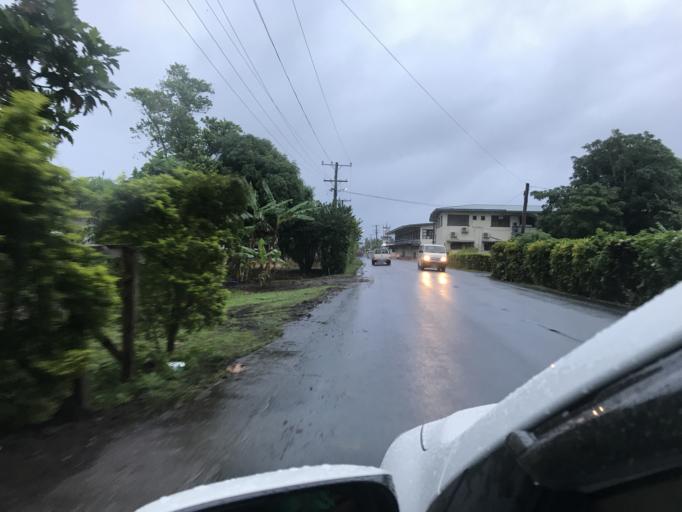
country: WS
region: Tuamasaga
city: Apia
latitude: -13.8343
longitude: -171.7550
